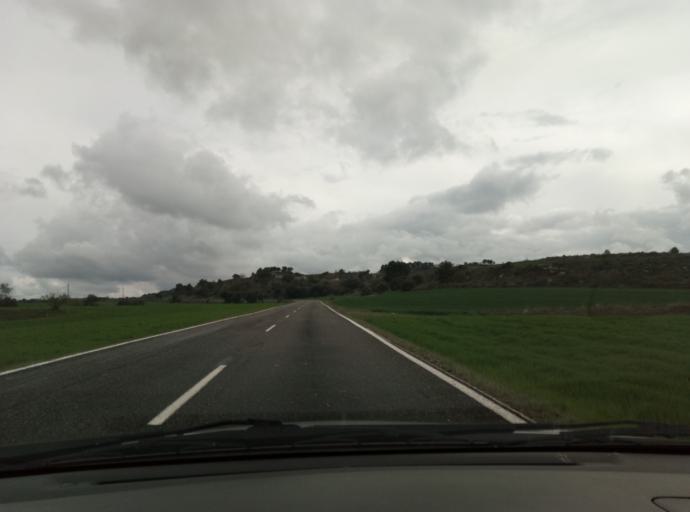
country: ES
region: Catalonia
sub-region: Provincia de Lleida
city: Sant Guim de Freixenet
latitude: 41.6154
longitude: 1.3431
